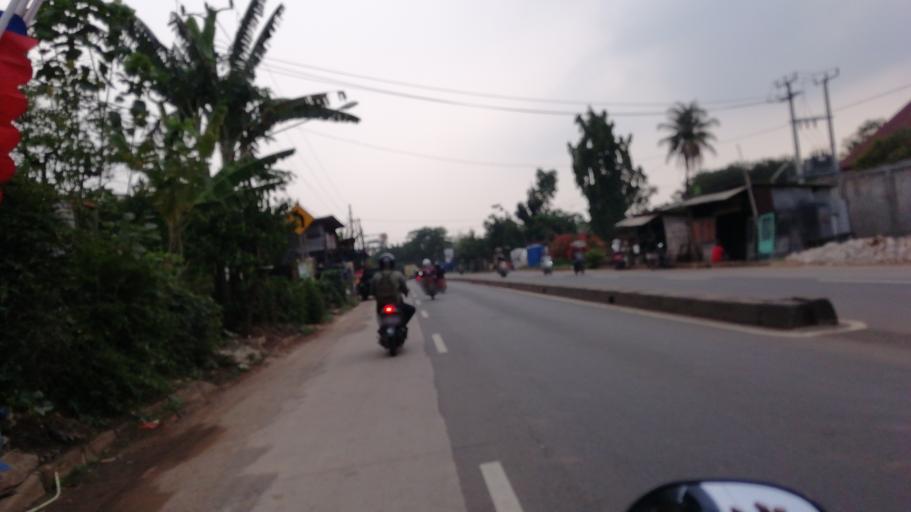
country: ID
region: West Java
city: Parung
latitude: -6.4643
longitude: 106.7295
